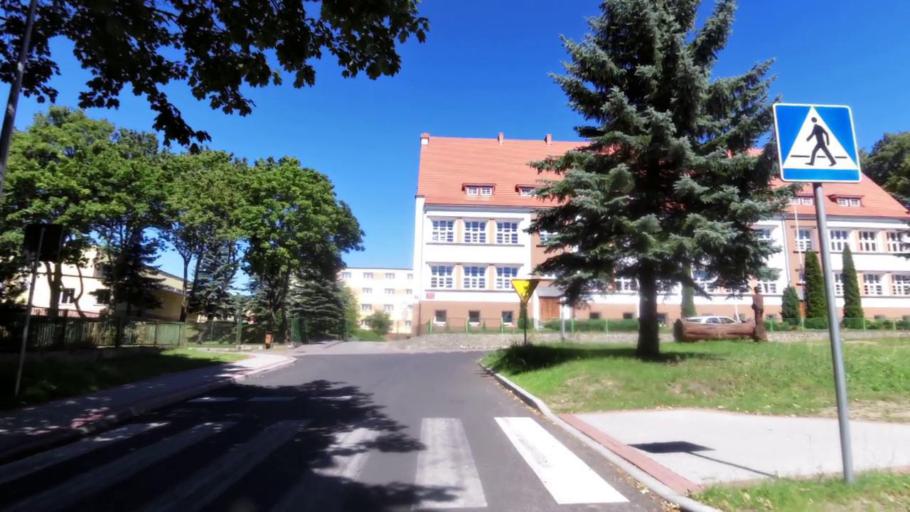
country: PL
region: West Pomeranian Voivodeship
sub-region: Powiat szczecinecki
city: Bialy Bor
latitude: 53.8952
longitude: 16.8419
